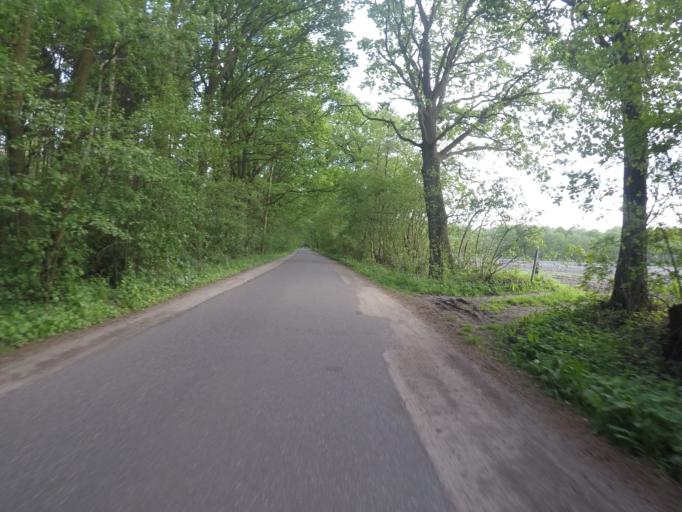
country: DE
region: Schleswig-Holstein
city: Bonningstedt
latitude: 53.6570
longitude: 9.9266
